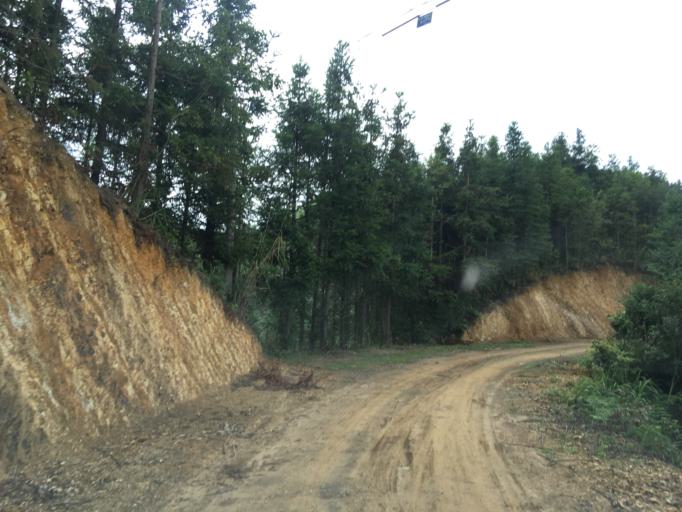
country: CN
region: Guangxi Zhuangzu Zizhiqu
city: Xinzhou
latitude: 24.8690
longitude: 105.8479
